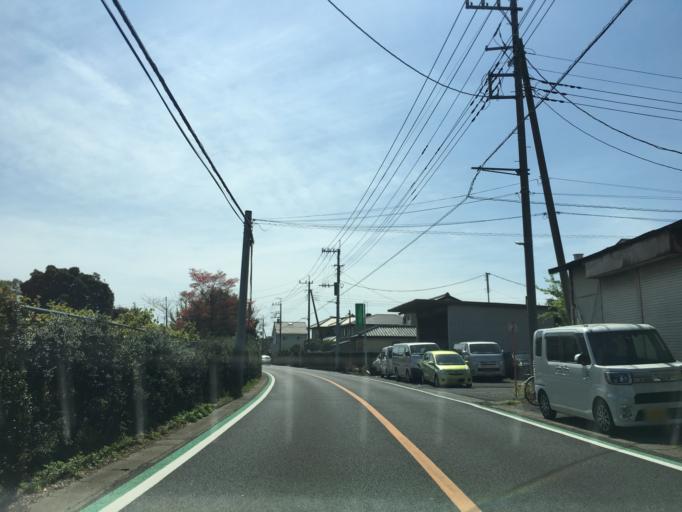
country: JP
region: Saitama
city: Sugito
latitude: 36.0082
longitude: 139.7155
